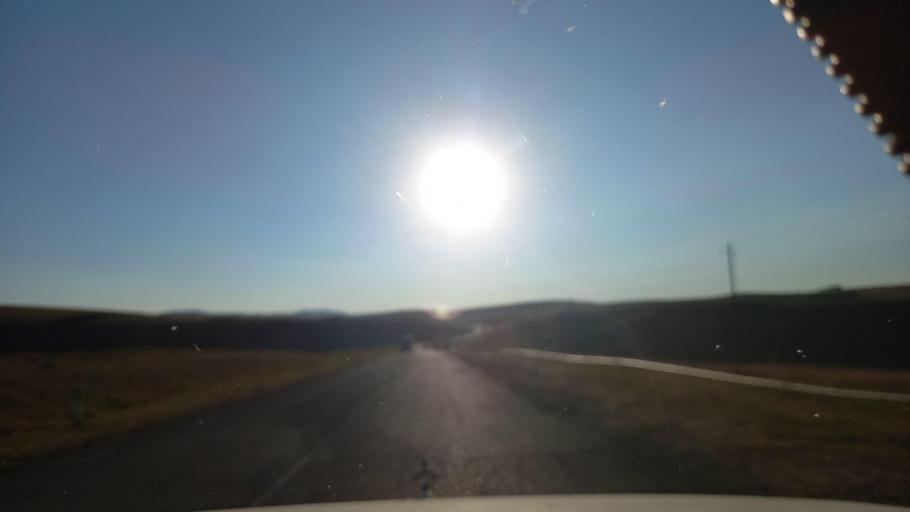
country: AZ
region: Shamkir Rayon
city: Shamkhor
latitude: 40.7639
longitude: 45.9319
